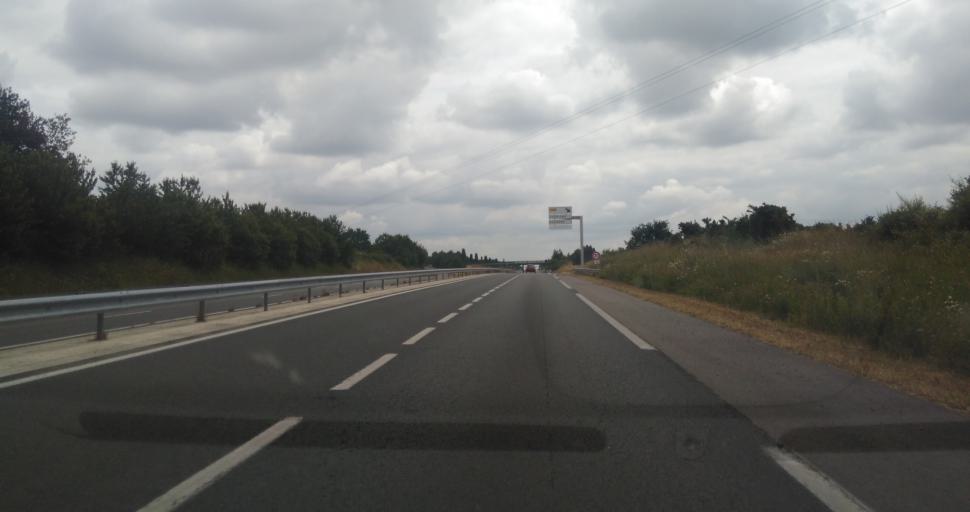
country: FR
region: Pays de la Loire
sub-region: Departement de la Vendee
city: La Chaize-le-Vicomte
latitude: 46.6547
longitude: -1.2360
